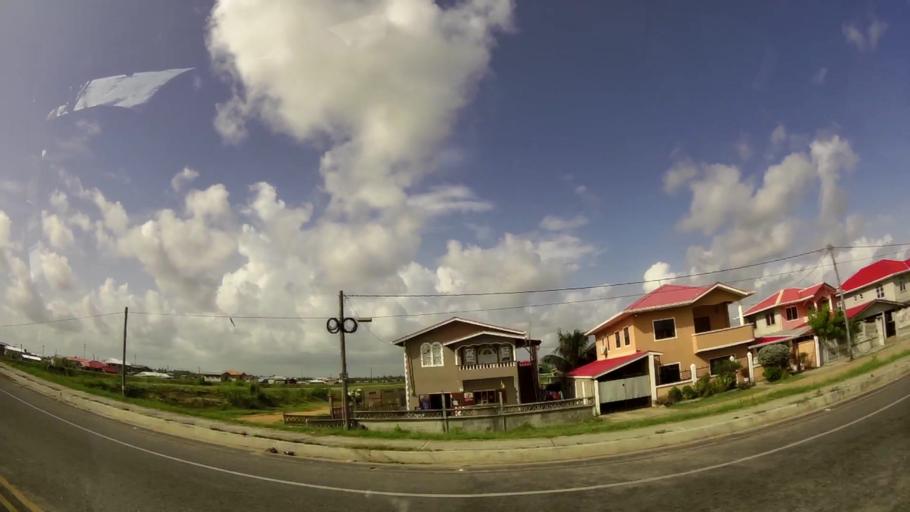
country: GY
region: Demerara-Mahaica
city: Mahaica Village
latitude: 6.7384
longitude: -57.9540
